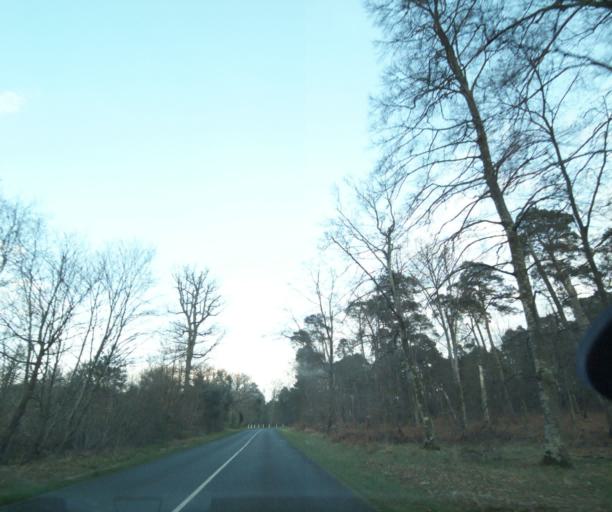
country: FR
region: Ile-de-France
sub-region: Departement de Seine-et-Marne
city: Montigny-sur-Loing
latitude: 48.3722
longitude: 2.7551
